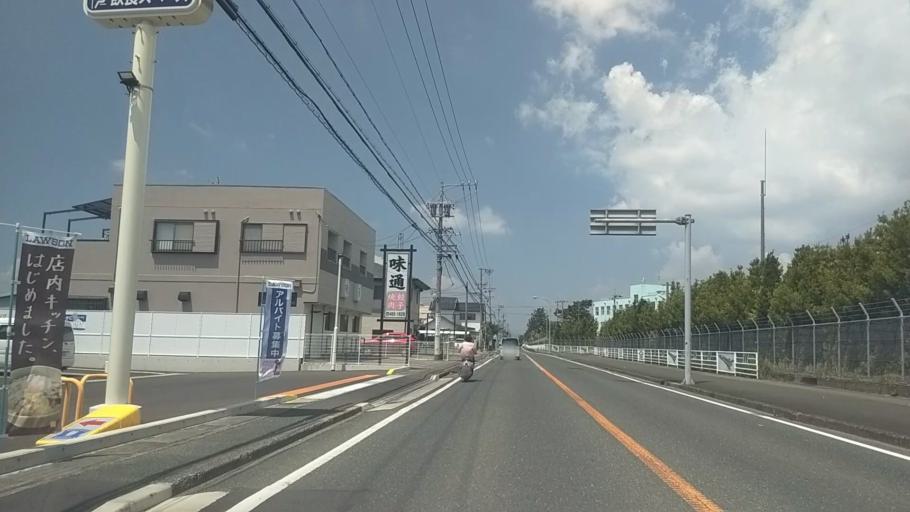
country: JP
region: Shizuoka
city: Hamamatsu
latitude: 34.7407
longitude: 137.6954
